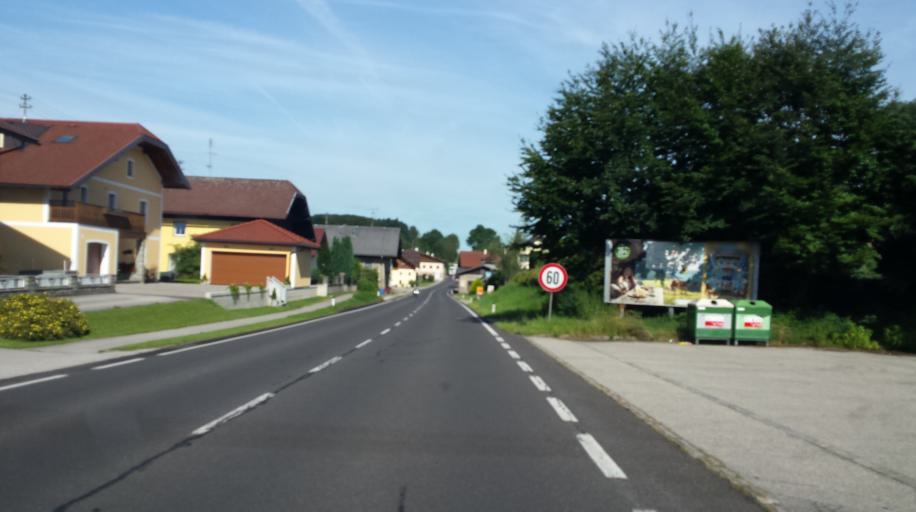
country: AT
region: Upper Austria
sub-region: Politischer Bezirk Vocklabruck
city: Frankenmarkt
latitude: 47.9931
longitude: 13.3536
